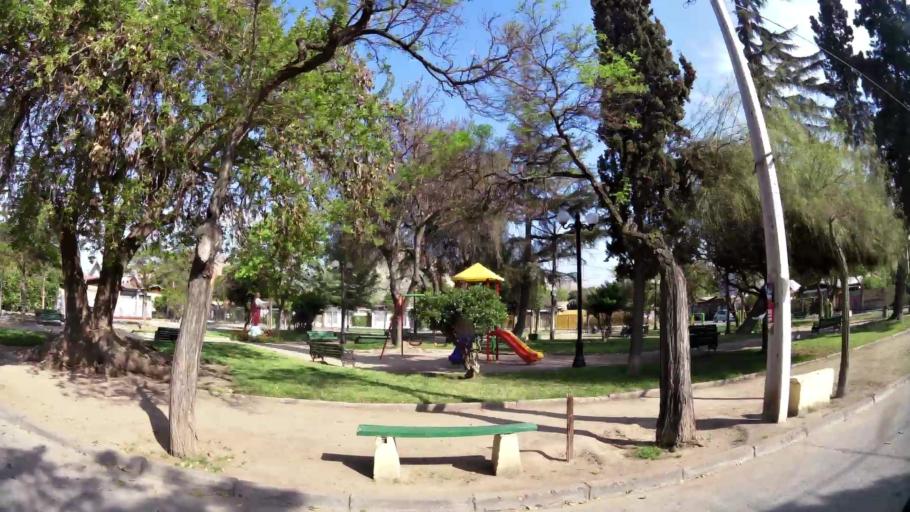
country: CL
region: Santiago Metropolitan
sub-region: Provincia de Maipo
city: San Bernardo
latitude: -33.5995
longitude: -70.7085
